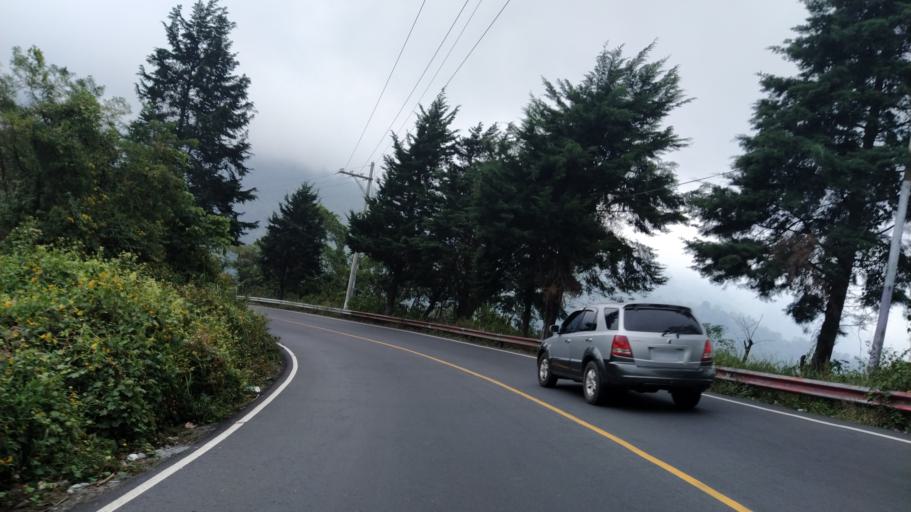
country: GT
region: Quetzaltenango
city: Zunil
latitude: 14.7325
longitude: -91.5238
